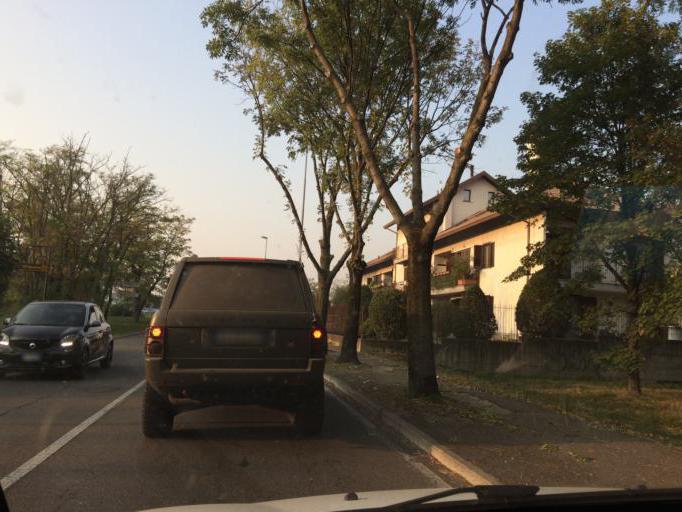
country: IT
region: Lombardy
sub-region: Provincia di Varese
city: Castellanza
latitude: 45.5951
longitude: 8.8976
